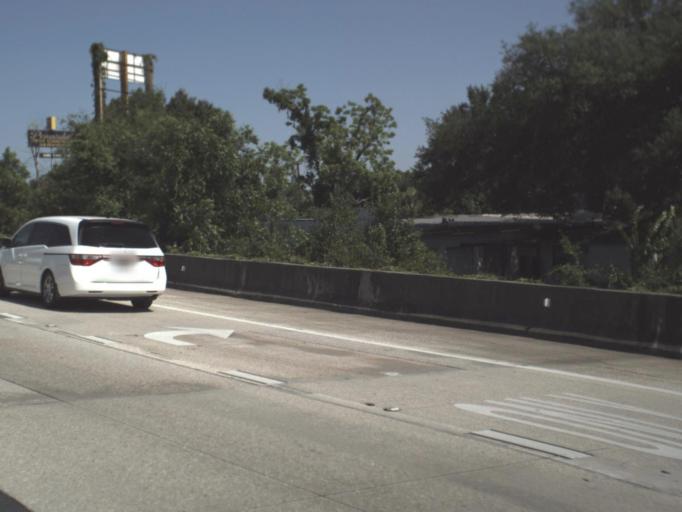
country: US
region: Florida
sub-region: Duval County
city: Jacksonville
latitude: 30.3215
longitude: -81.6953
